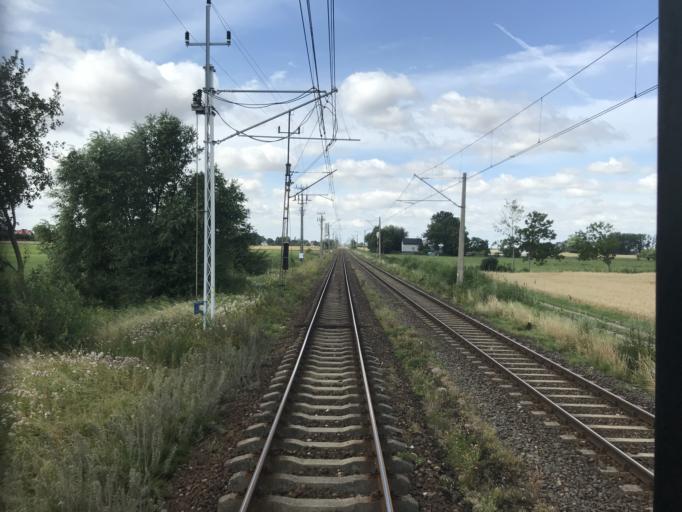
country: PL
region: Warmian-Masurian Voivodeship
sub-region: Powiat elblaski
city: Gronowo Elblaskie
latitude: 54.0865
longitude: 19.2972
